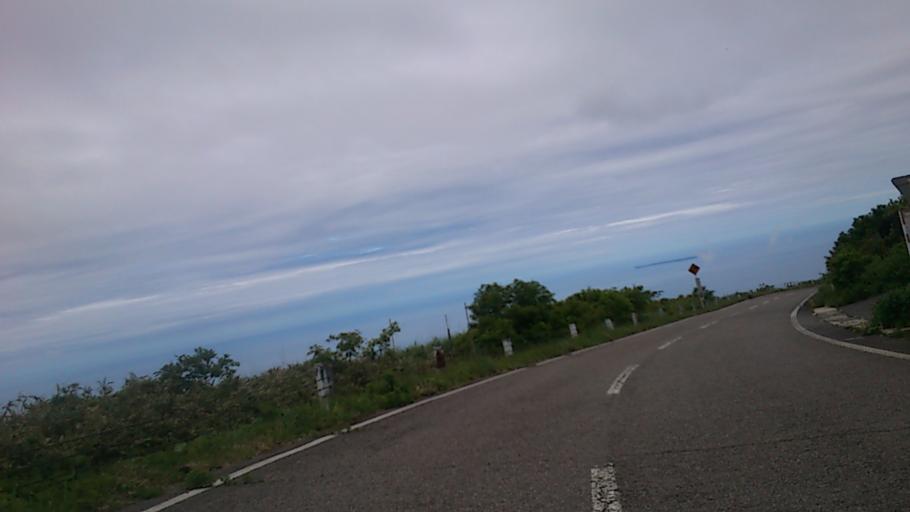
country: JP
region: Yamagata
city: Yuza
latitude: 39.1066
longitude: 139.9770
